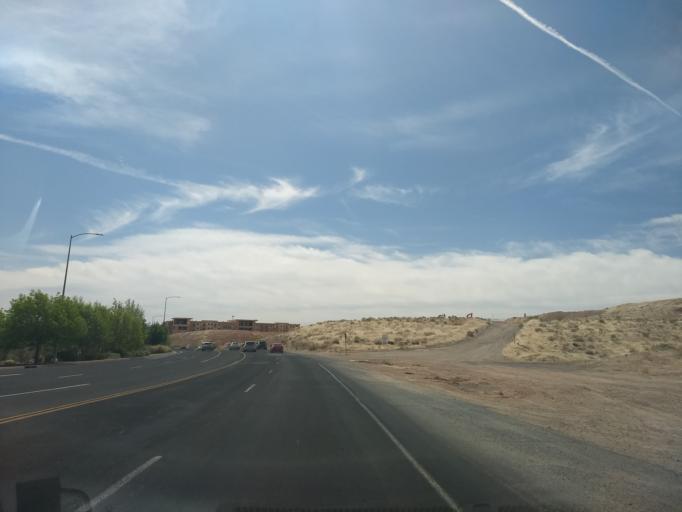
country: US
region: Utah
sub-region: Washington County
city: Saint George
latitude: 37.0917
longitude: -113.6155
